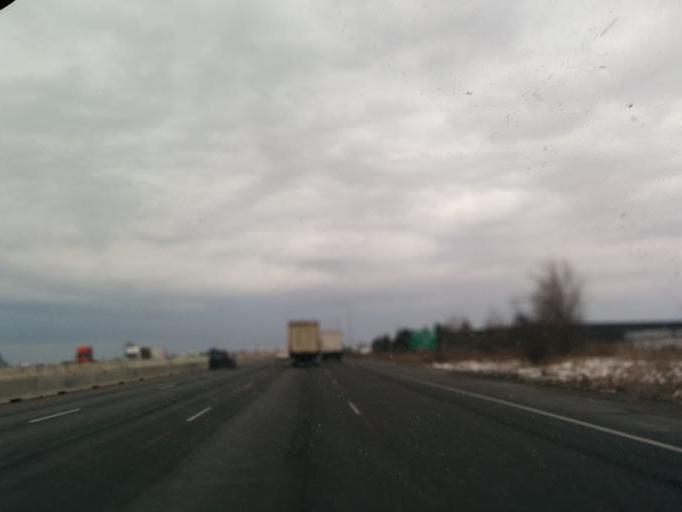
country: CA
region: Ontario
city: Etobicoke
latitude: 43.7128
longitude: -79.6172
